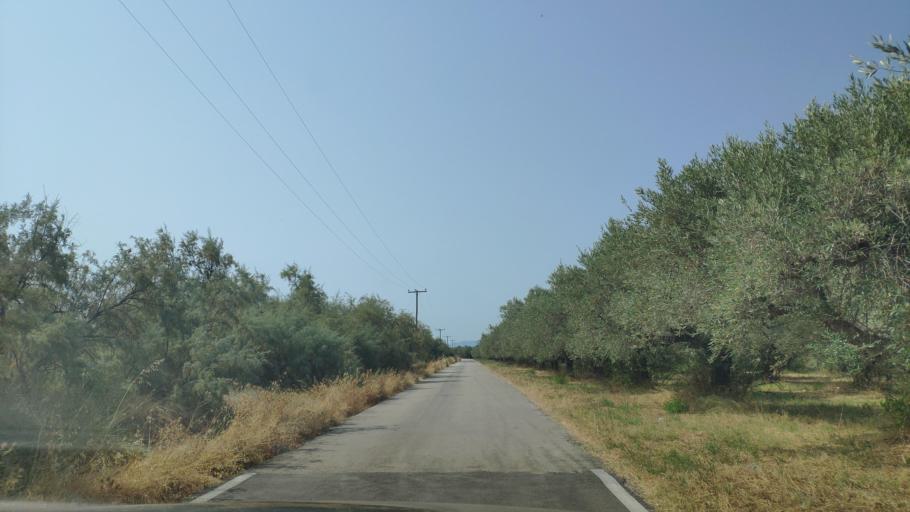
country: GR
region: West Greece
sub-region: Nomos Aitolias kai Akarnanias
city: Menidi
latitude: 39.0472
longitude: 21.0722
